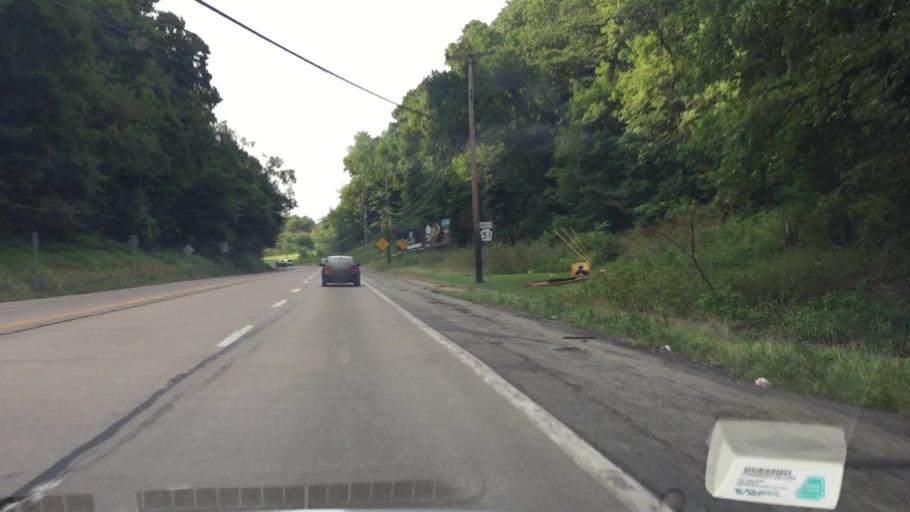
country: US
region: Pennsylvania
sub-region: Allegheny County
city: Edgeworth
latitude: 40.5396
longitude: -80.2010
